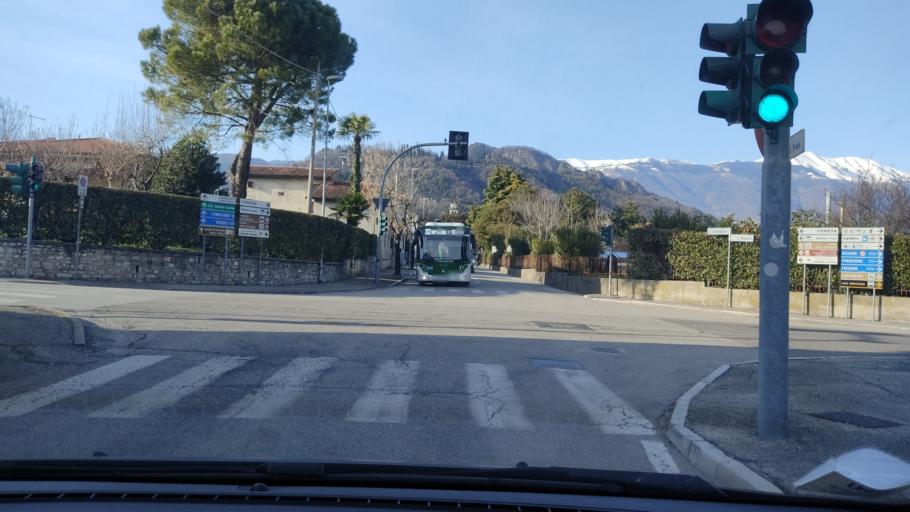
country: IT
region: Veneto
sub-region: Provincia di Treviso
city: Vittorio Veneto
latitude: 45.9712
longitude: 12.2970
